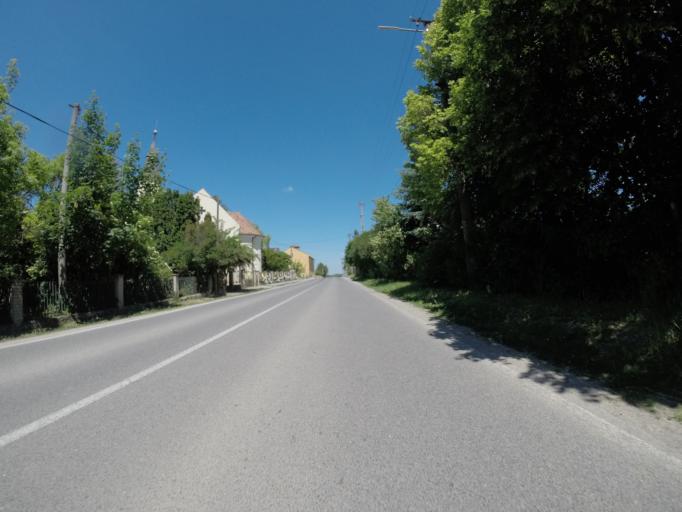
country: SK
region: Trnavsky
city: Hlohovec
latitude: 48.4610
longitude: 17.9425
